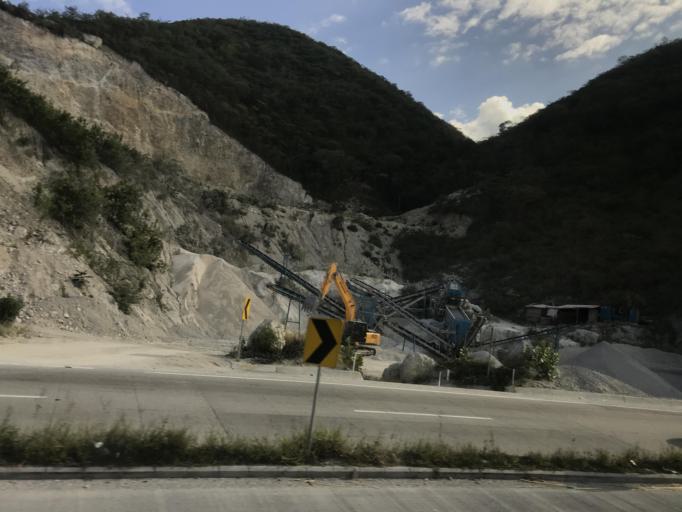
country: GT
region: El Progreso
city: Guastatoya
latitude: 14.8468
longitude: -90.1126
